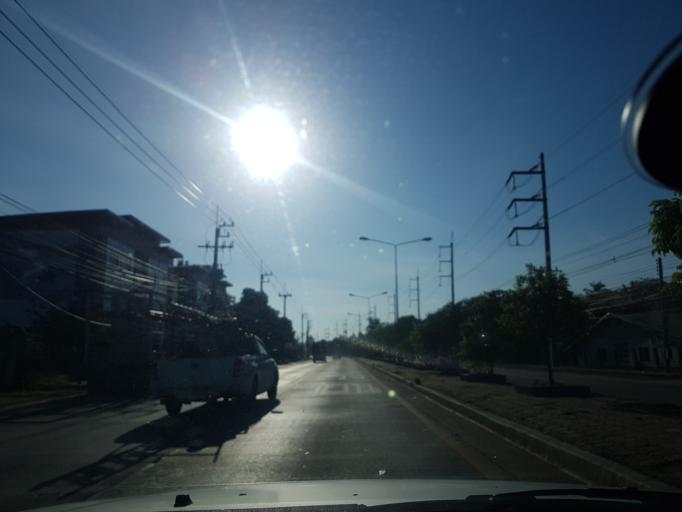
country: TH
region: Lop Buri
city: Lop Buri
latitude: 14.7718
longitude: 100.7013
